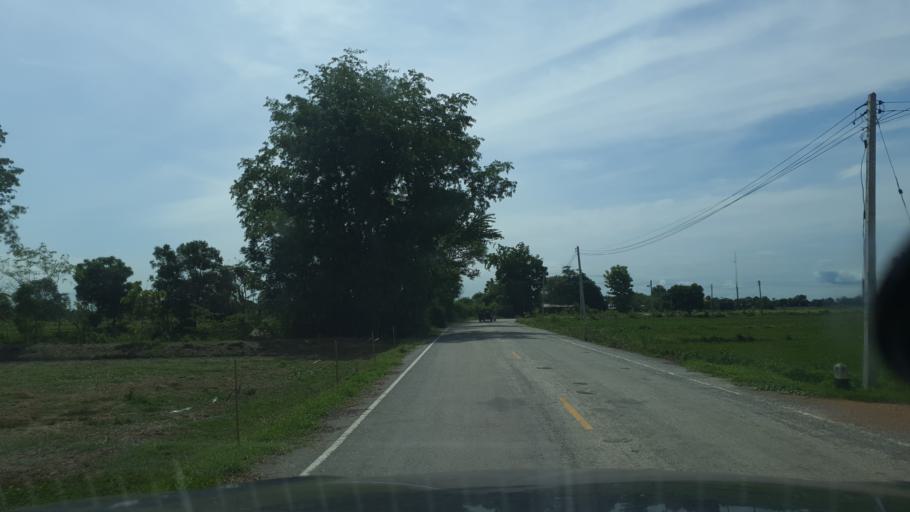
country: TH
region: Sukhothai
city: Si Samrong
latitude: 17.1975
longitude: 99.7247
